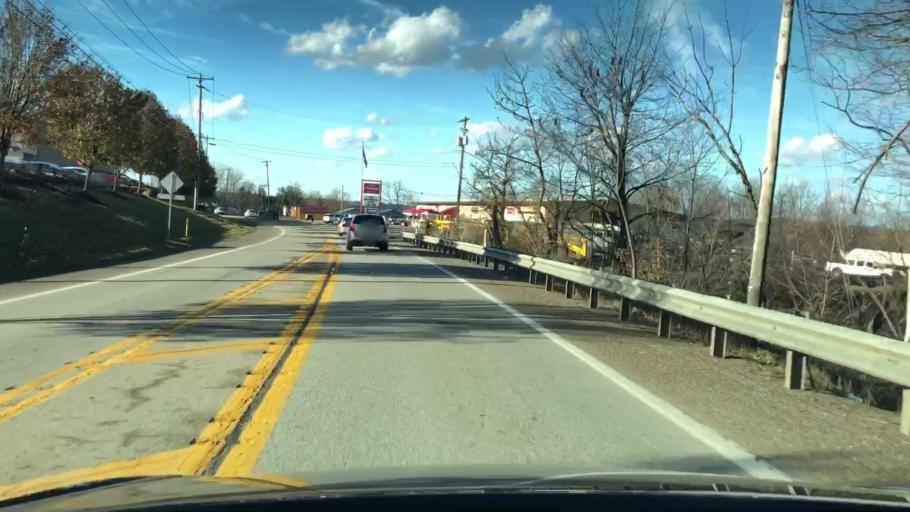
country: US
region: Pennsylvania
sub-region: Armstrong County
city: Freeport
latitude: 40.7068
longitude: -79.7246
